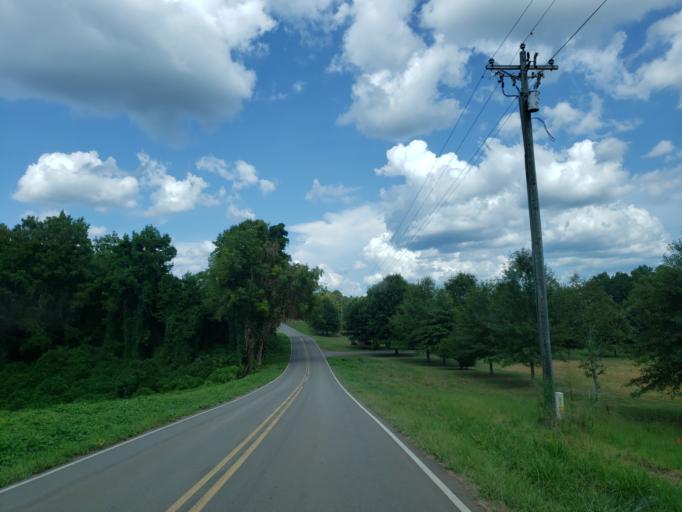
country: US
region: Georgia
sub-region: Pickens County
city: Jasper
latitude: 34.4284
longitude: -84.4389
